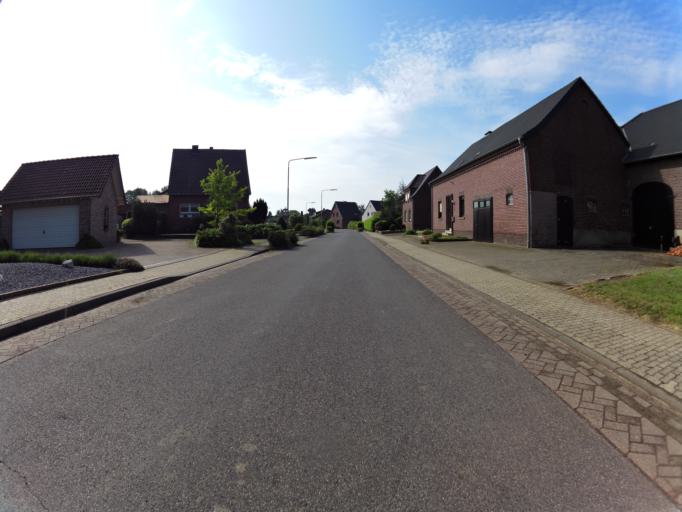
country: DE
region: North Rhine-Westphalia
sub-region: Regierungsbezirk Koln
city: Waldfeucht
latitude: 51.0775
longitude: 5.9932
